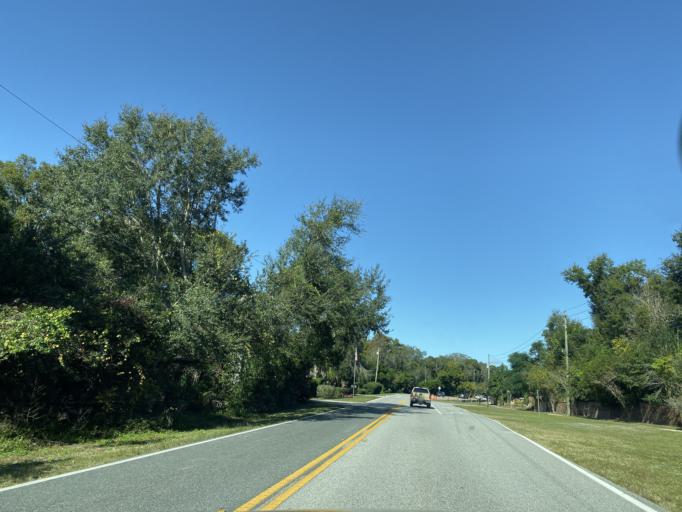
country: US
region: Florida
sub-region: Seminole County
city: Goldenrod
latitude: 28.6083
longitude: -81.2437
